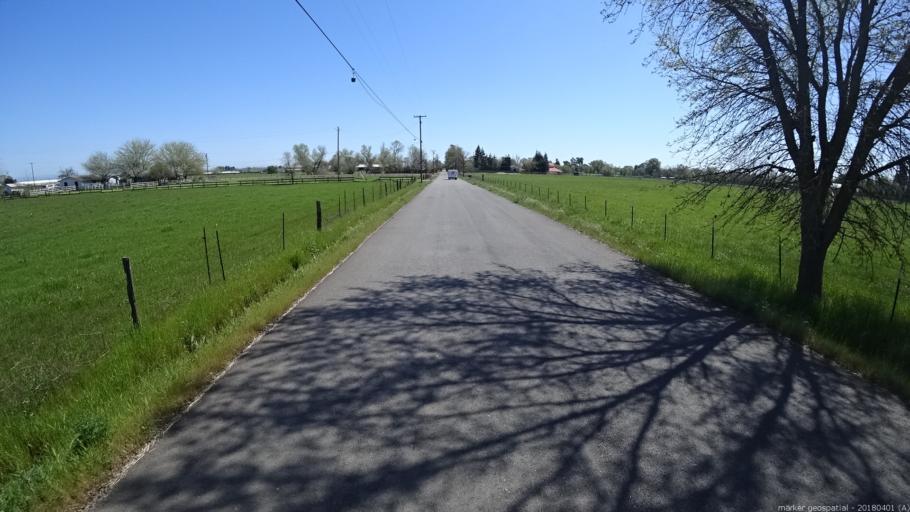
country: US
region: California
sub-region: Sacramento County
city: Rancho Murieta
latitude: 38.4513
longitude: -121.1719
